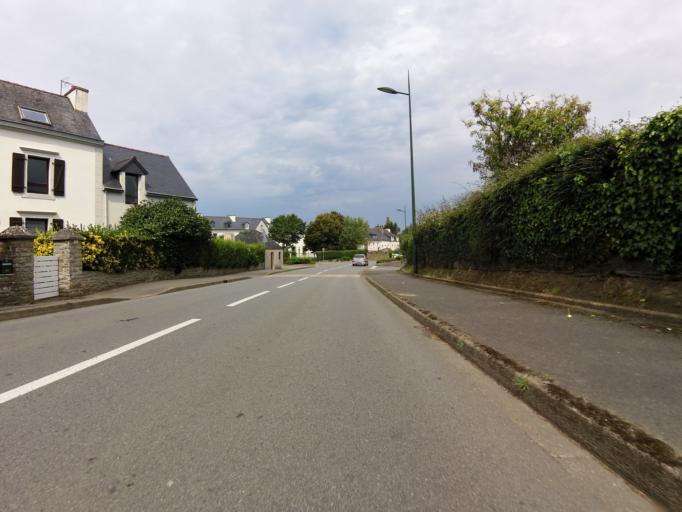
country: FR
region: Brittany
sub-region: Departement du Finistere
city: Poullan-sur-Mer
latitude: 48.0810
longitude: -4.4125
